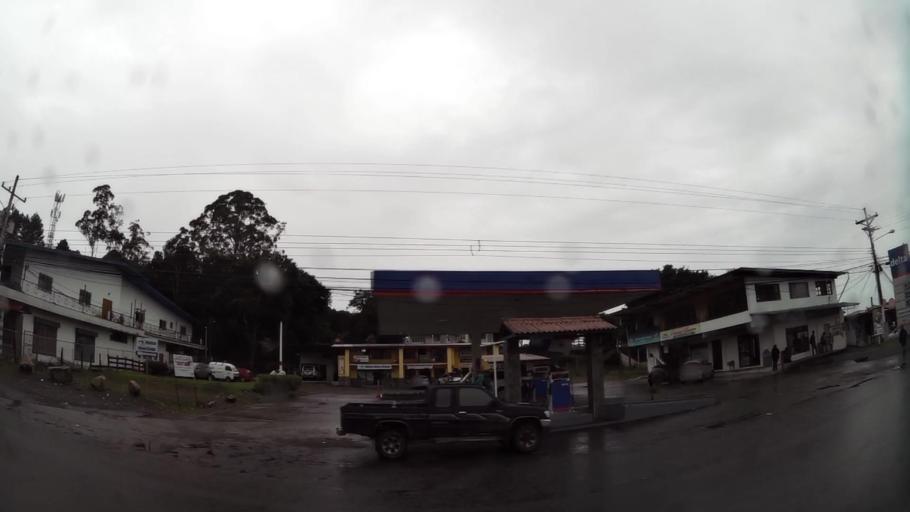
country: PA
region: Chiriqui
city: Volcan
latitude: 8.7759
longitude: -82.6401
